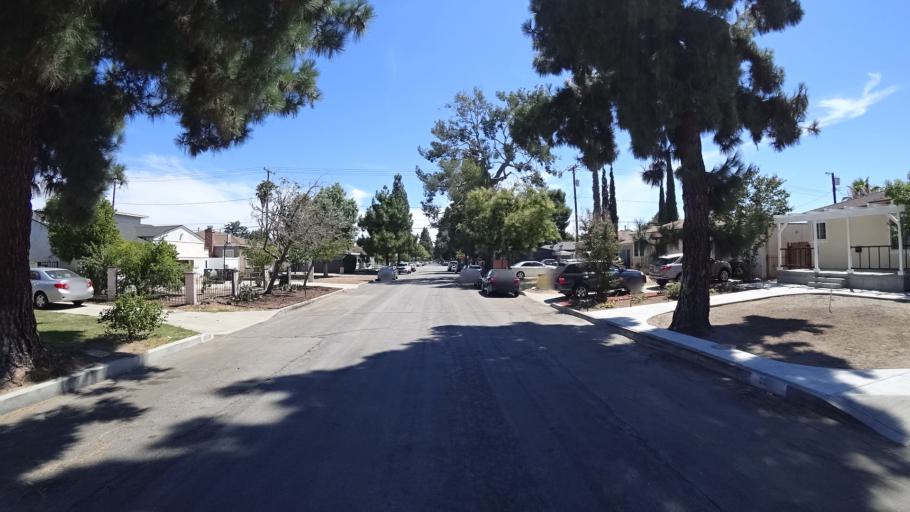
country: US
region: California
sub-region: Los Angeles County
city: North Hollywood
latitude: 34.1857
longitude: -118.3545
